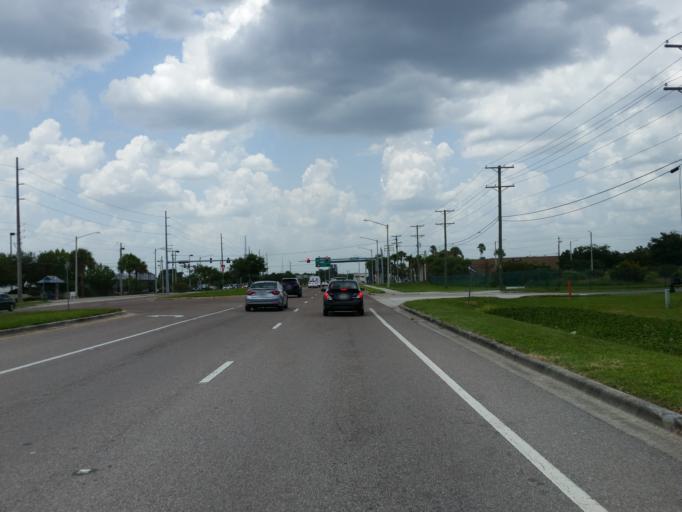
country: US
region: Florida
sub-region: Hillsborough County
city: Brandon
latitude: 27.9188
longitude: -82.3185
